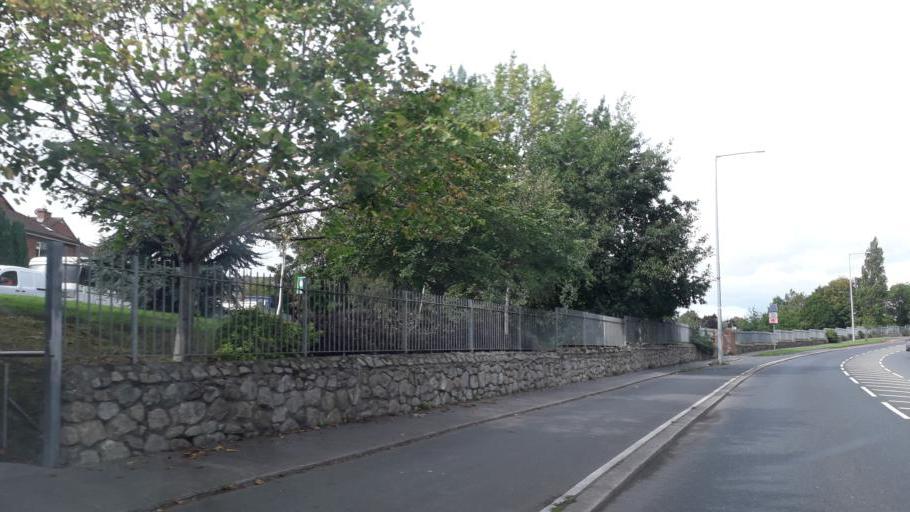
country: IE
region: Leinster
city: Cabinteely
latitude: 53.2654
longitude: -6.1483
